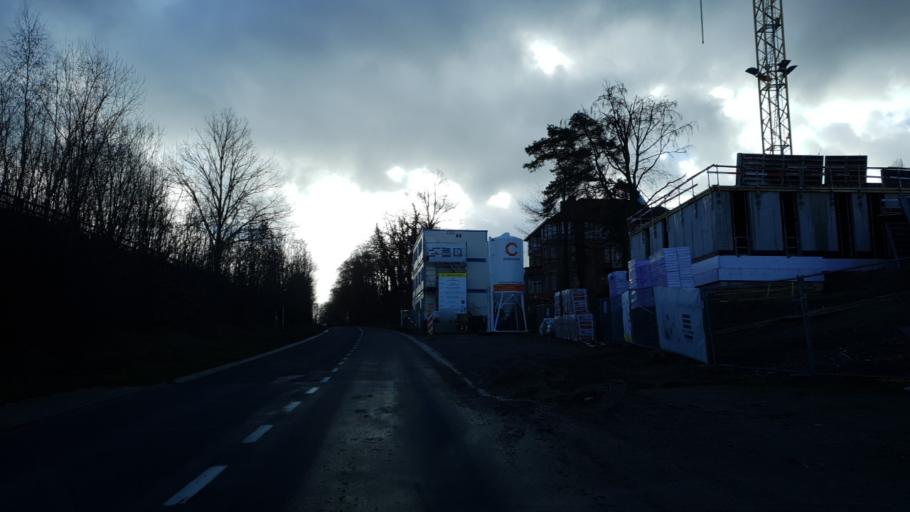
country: BE
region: Flanders
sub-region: Provincie Vlaams-Brabant
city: Kortenberg
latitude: 50.8702
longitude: 4.5794
